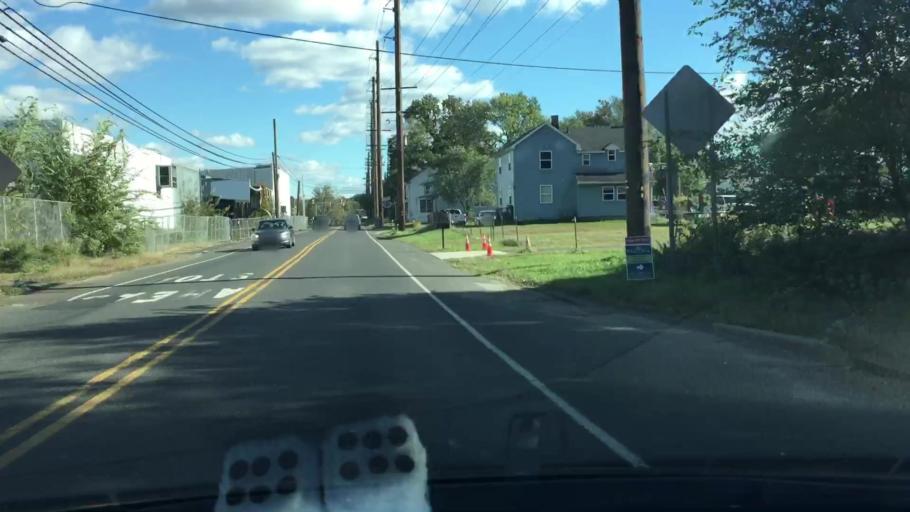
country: US
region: New Jersey
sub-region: Gloucester County
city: Turnersville
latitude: 39.7746
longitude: -75.0538
